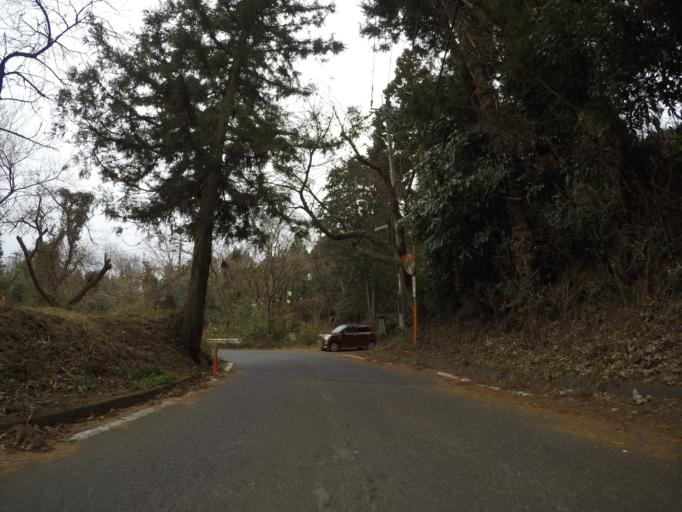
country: JP
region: Shizuoka
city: Fujinomiya
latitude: 35.2592
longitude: 138.5496
